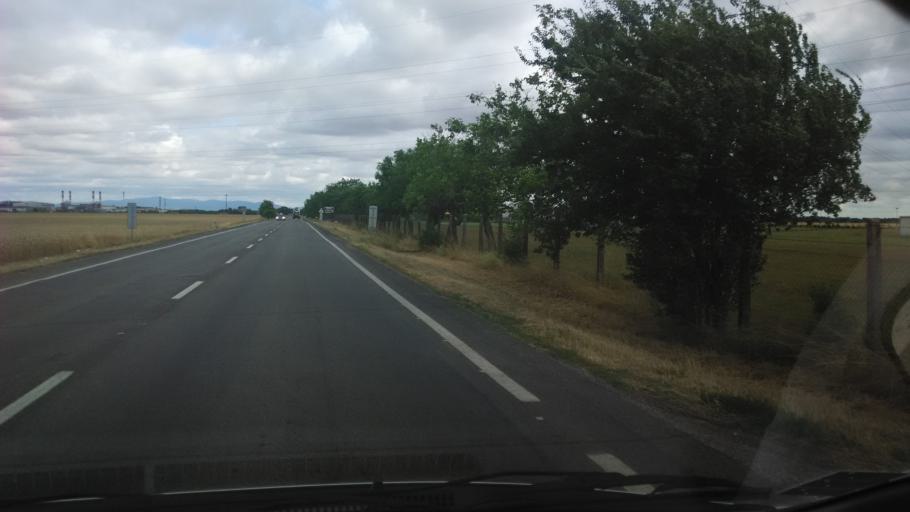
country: SK
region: Nitriansky
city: Levice
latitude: 48.2025
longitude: 18.5843
